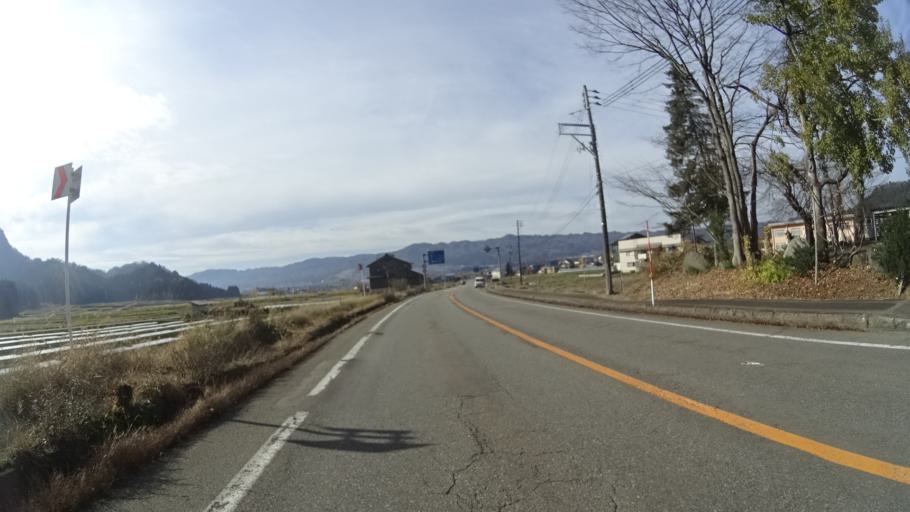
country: JP
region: Niigata
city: Muikamachi
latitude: 37.1285
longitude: 138.9456
